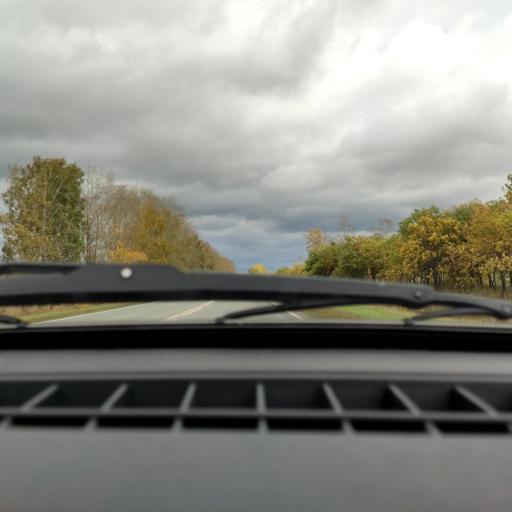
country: RU
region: Bashkortostan
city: Shafranovo
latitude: 54.0142
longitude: 54.8235
